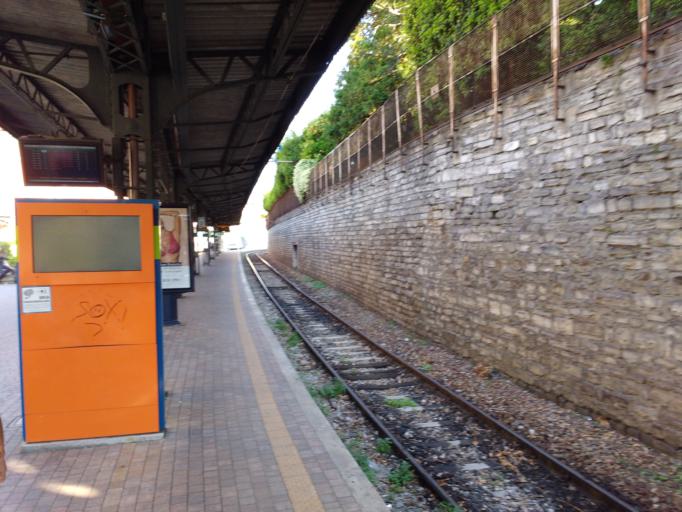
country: IT
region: Lombardy
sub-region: Provincia di Como
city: Como
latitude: 45.8145
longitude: 9.0835
